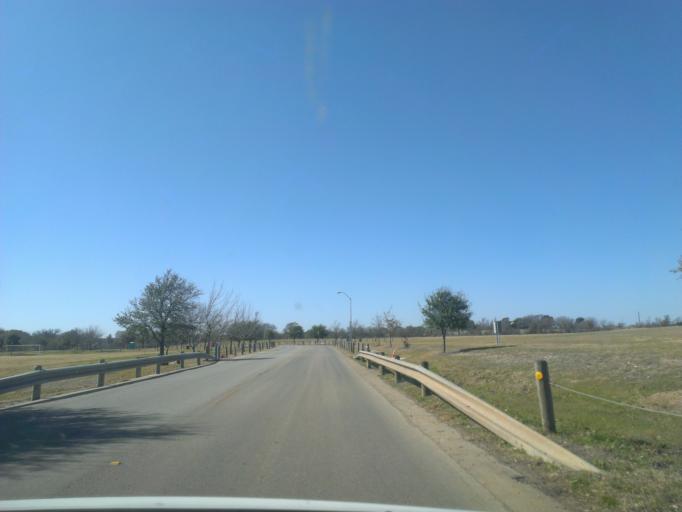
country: US
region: Texas
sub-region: Williamson County
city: Round Rock
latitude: 30.5328
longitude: -97.6313
